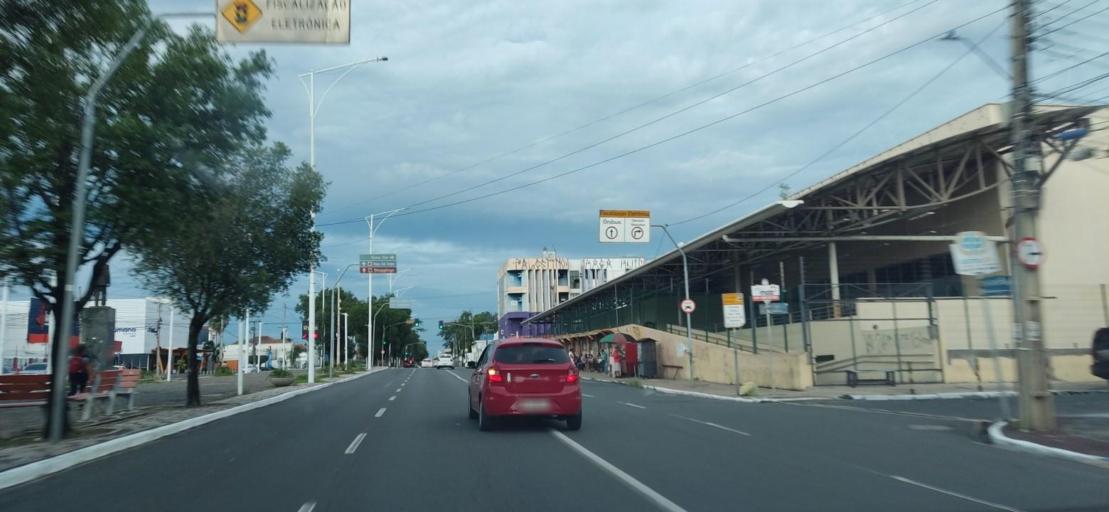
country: BR
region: Piaui
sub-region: Teresina
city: Teresina
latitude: -5.0887
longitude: -42.8073
